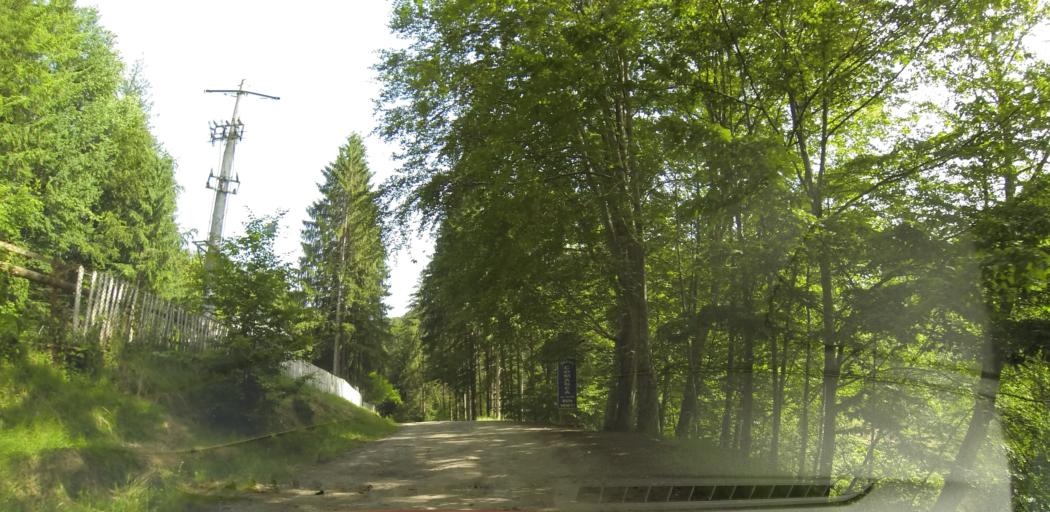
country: RO
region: Valcea
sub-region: Oras Baile Olanesti
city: Baile Olanesti
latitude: 45.2218
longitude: 24.2114
